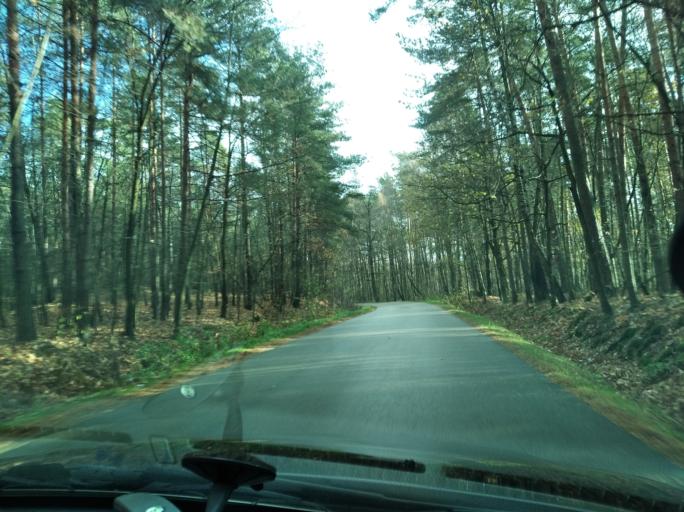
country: PL
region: Subcarpathian Voivodeship
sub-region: Powiat ropczycko-sedziszowski
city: Sedziszow Malopolski
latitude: 50.1210
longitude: 21.7164
